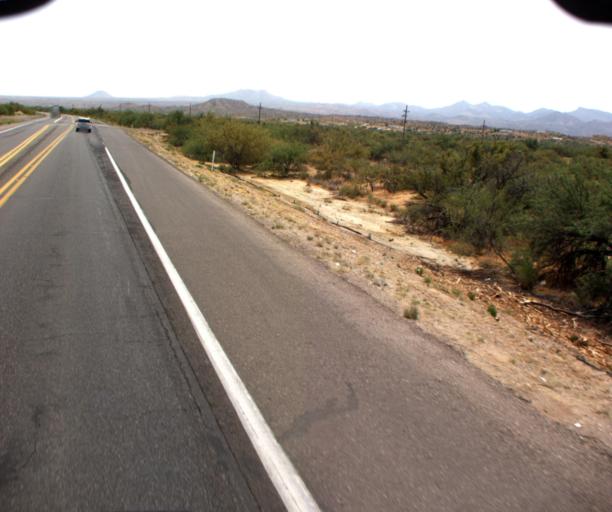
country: US
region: Arizona
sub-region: Gila County
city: Globe
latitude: 33.3603
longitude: -110.6999
